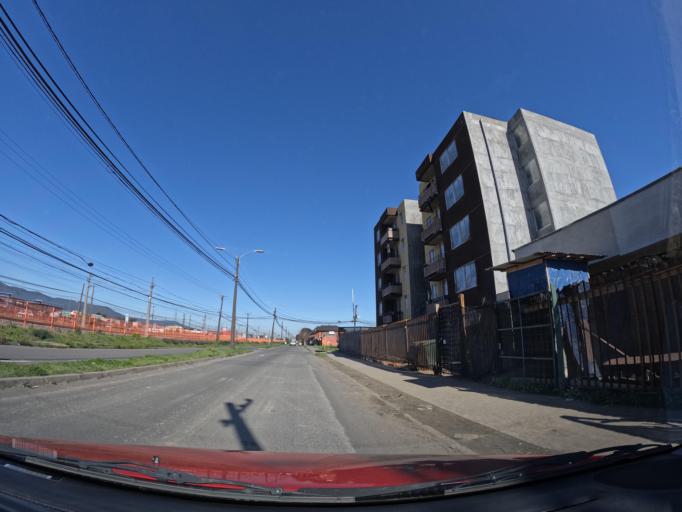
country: CL
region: Biobio
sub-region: Provincia de Concepcion
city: Concepcion
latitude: -36.8855
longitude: -73.1408
